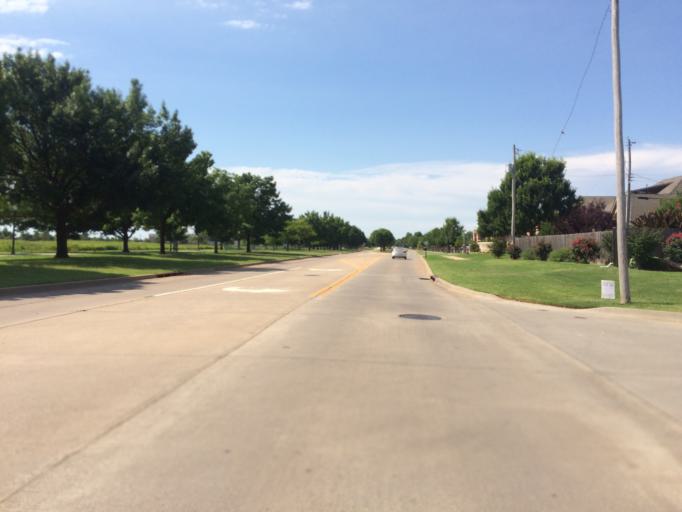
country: US
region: Oklahoma
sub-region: Cleveland County
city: Norman
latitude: 35.1932
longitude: -97.4501
